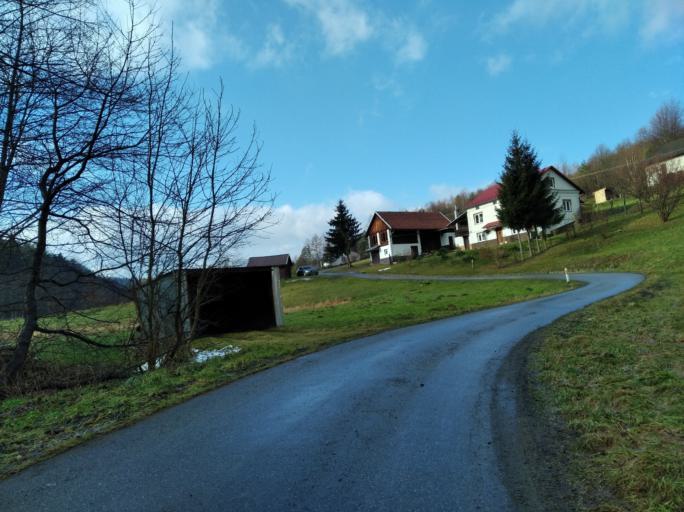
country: PL
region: Subcarpathian Voivodeship
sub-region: Powiat strzyzowski
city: Jawornik
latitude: 49.8326
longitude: 21.8797
